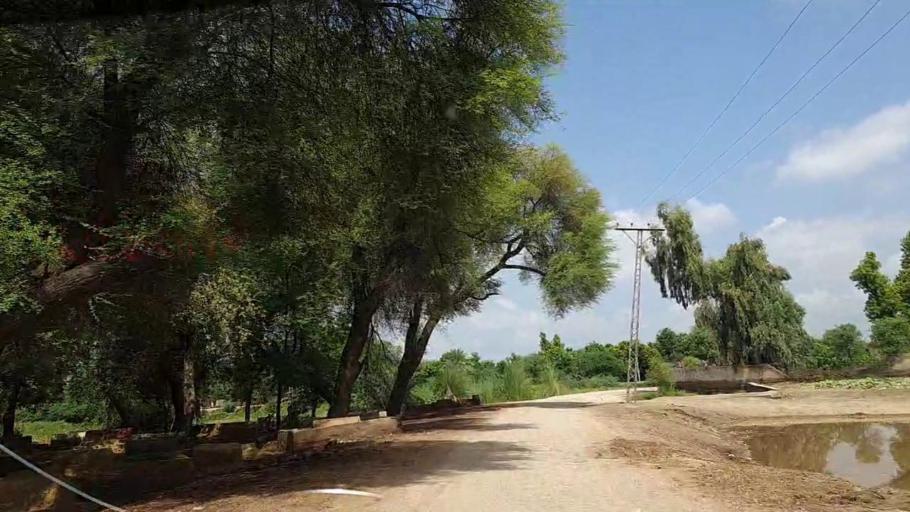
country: PK
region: Sindh
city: Tharu Shah
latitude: 26.9120
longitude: 68.0332
